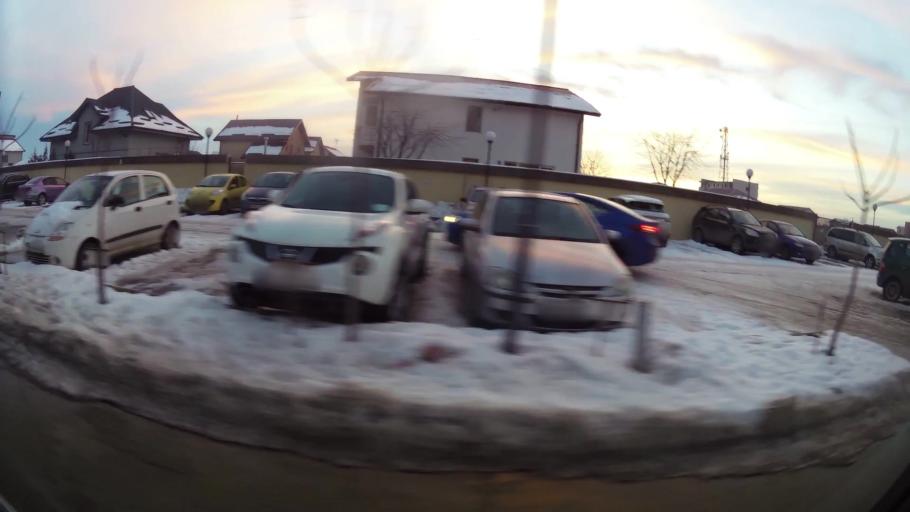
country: RO
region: Ilfov
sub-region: Comuna Magurele
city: Magurele
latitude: 44.3877
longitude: 26.0247
